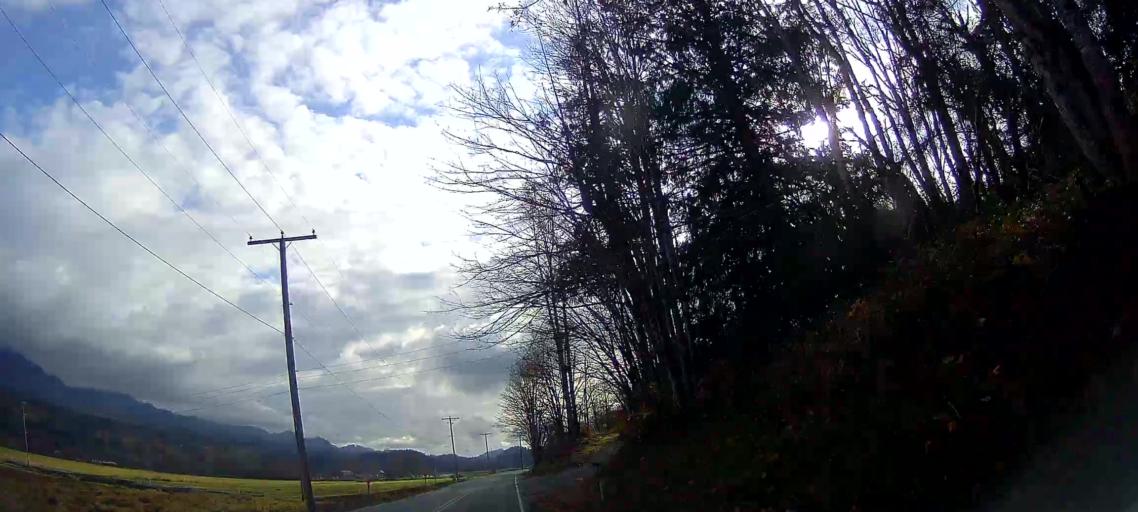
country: US
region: Washington
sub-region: Skagit County
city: Clear Lake
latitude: 48.4433
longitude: -122.2200
